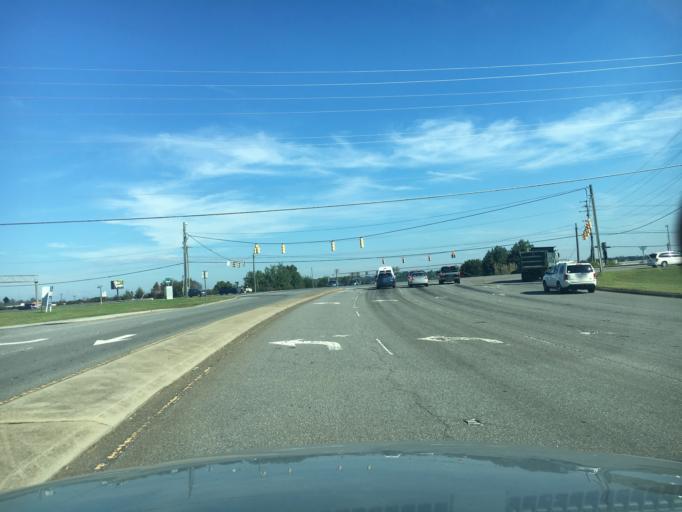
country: US
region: North Carolina
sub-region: Catawba County
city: Hickory
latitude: 35.7015
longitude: -81.2942
